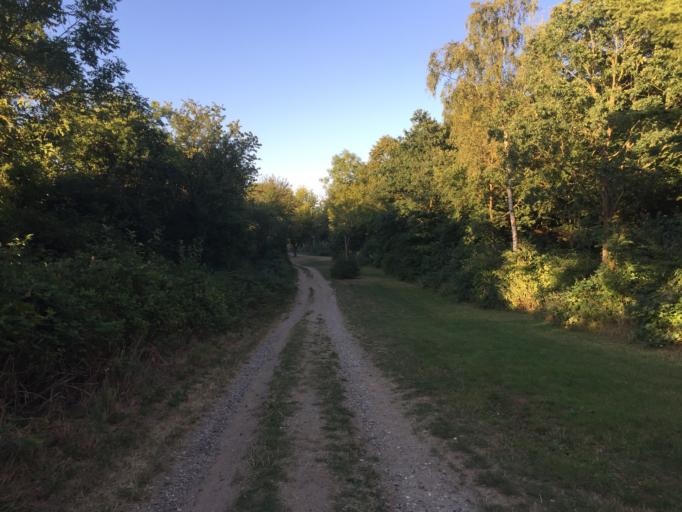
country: DK
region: South Denmark
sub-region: Odense Kommune
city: Odense
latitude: 55.3847
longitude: 10.3397
